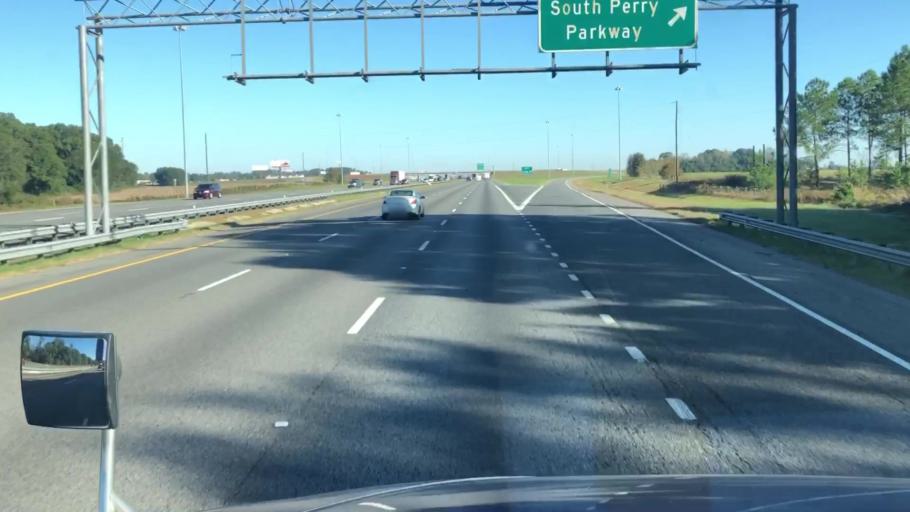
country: US
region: Georgia
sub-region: Houston County
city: Perry
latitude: 32.4234
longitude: -83.7593
